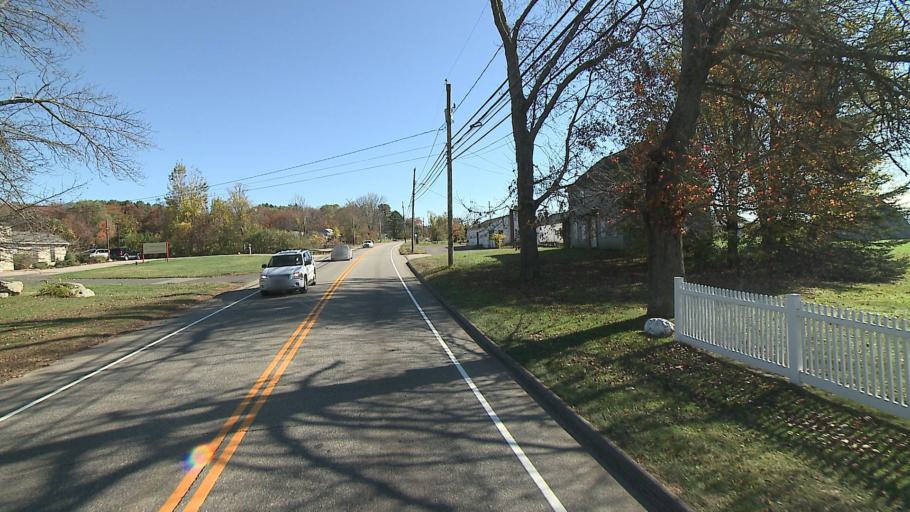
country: US
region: Connecticut
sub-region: Tolland County
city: Rockville
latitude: 41.7971
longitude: -72.4211
